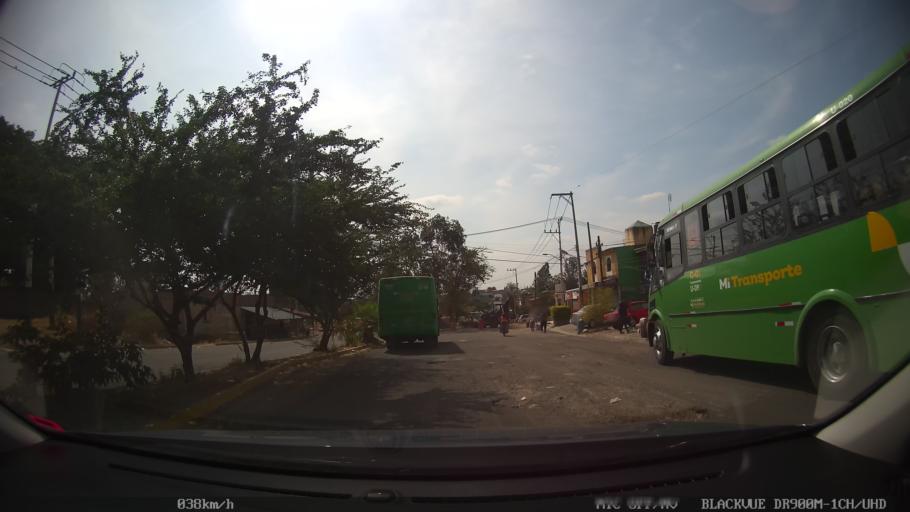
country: MX
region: Jalisco
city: Coyula
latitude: 20.6514
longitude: -103.2165
